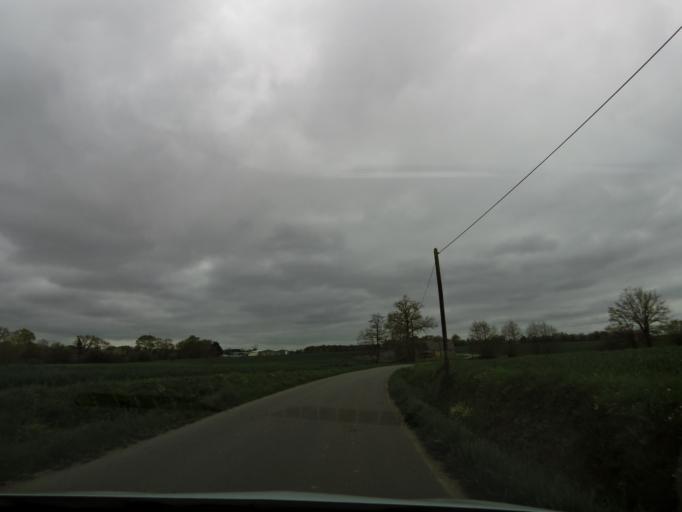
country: FR
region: Brittany
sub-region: Departement d'Ille-et-Vilaine
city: Janze
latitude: 47.9839
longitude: -1.5292
